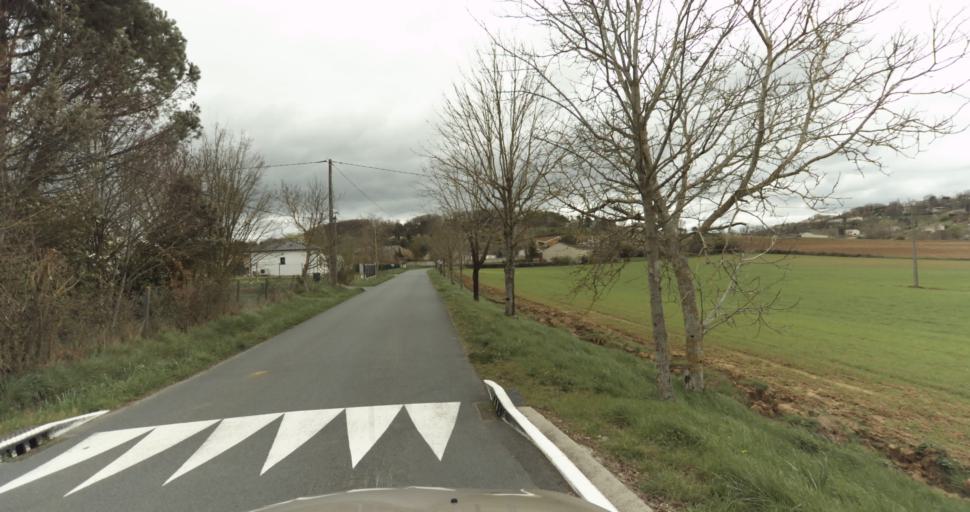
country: FR
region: Midi-Pyrenees
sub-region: Departement du Tarn
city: Puygouzon
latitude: 43.9082
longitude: 2.1723
